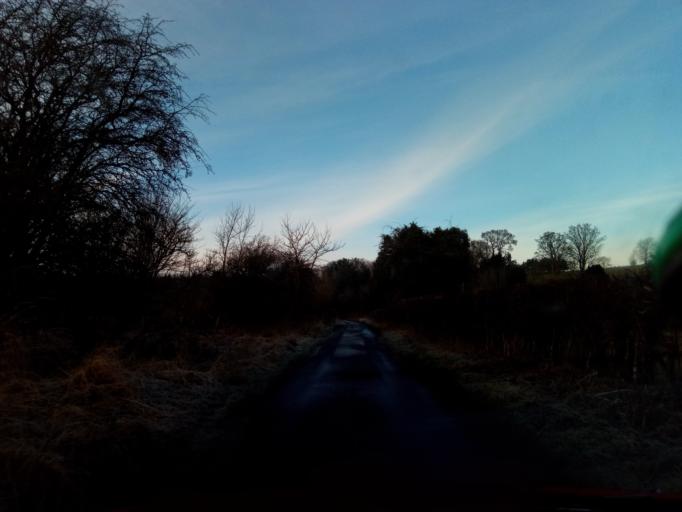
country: GB
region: Scotland
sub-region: The Scottish Borders
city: Hawick
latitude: 55.4542
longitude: -2.7161
